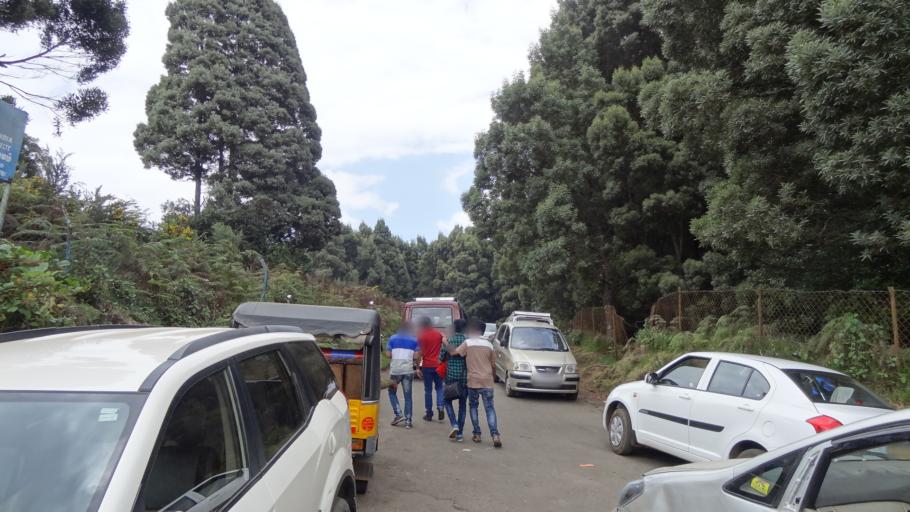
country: IN
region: Tamil Nadu
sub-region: Nilgiri
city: Aravankadu
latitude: 11.4017
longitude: 76.7364
